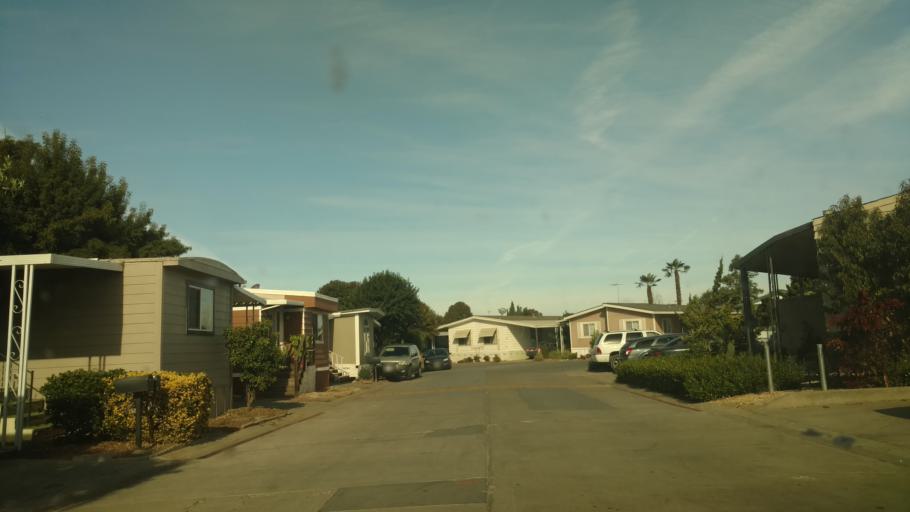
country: US
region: California
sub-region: San Benito County
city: Hollister
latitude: 36.8508
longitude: -121.4226
